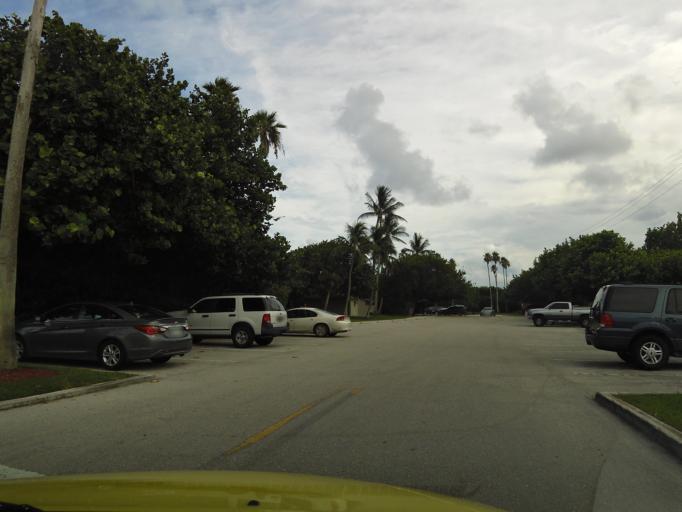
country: US
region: Florida
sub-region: Palm Beach County
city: Jupiter
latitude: 26.9635
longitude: -80.0792
